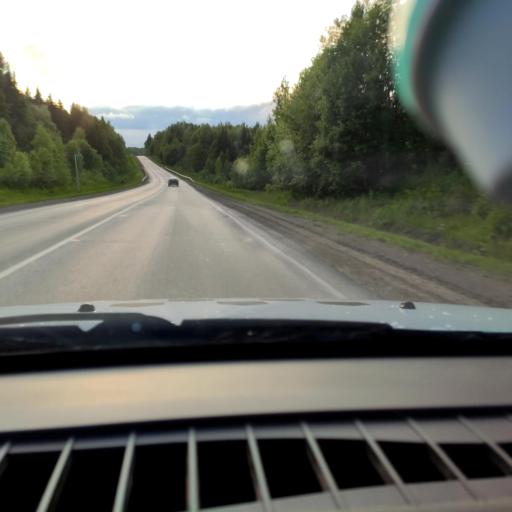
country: RU
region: Perm
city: Novyye Lyady
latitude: 58.2940
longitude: 56.6873
